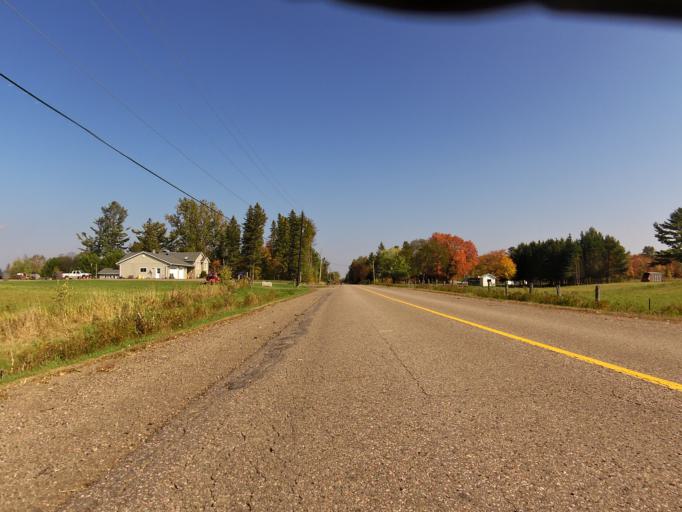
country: CA
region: Ontario
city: Petawawa
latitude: 45.8216
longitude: -77.2281
